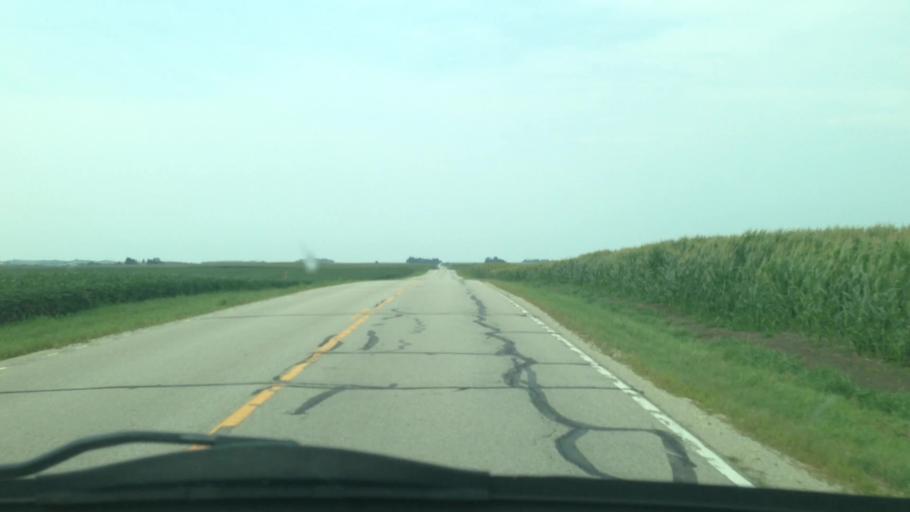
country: US
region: Minnesota
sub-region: Fillmore County
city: Preston
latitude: 43.7822
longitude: -91.9498
